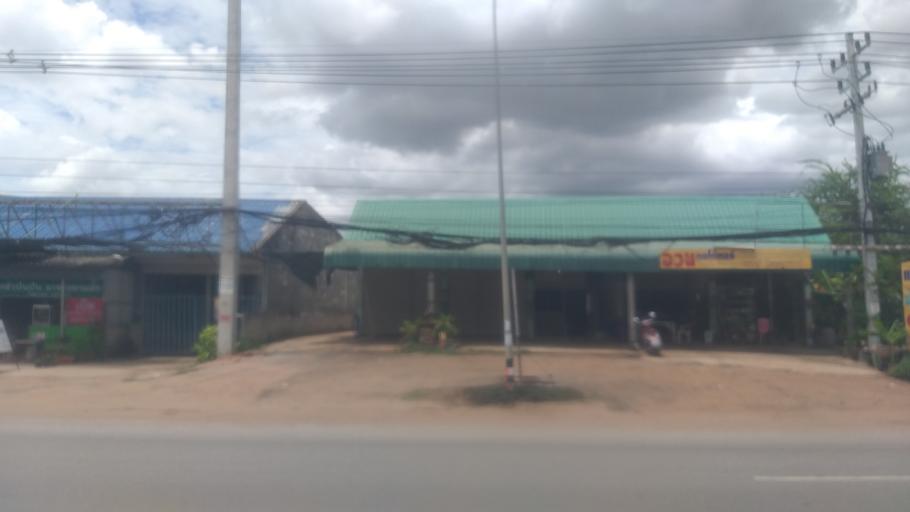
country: TH
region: Nakhon Ratchasima
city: Nakhon Ratchasima
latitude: 15.0683
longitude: 102.1206
